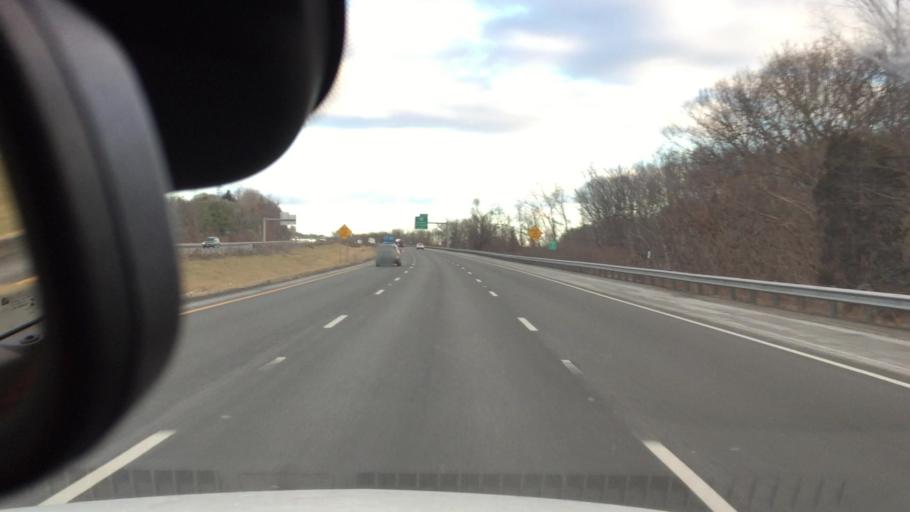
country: US
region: Massachusetts
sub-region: Hampden County
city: Holyoke
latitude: 42.1877
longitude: -72.6387
